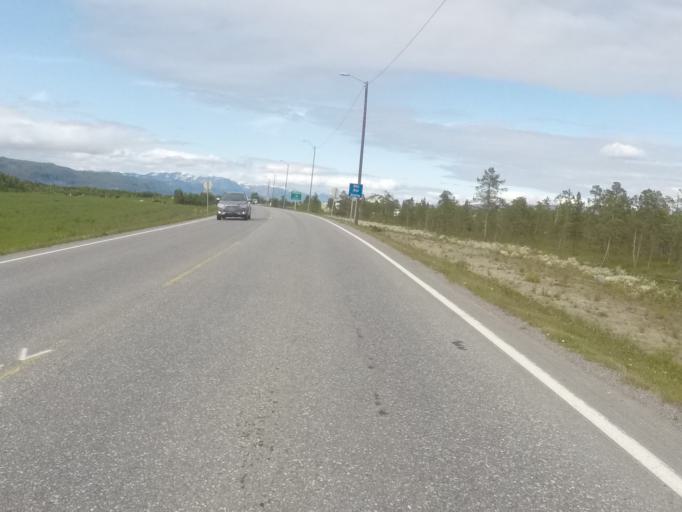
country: NO
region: Finnmark Fylke
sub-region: Alta
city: Alta
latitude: 69.9470
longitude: 23.2410
